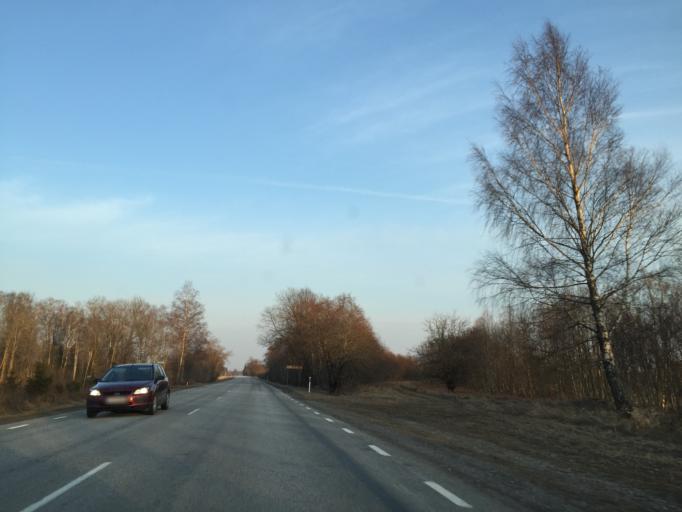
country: EE
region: Laeaene
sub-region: Lihula vald
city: Lihula
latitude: 58.5360
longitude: 24.0242
